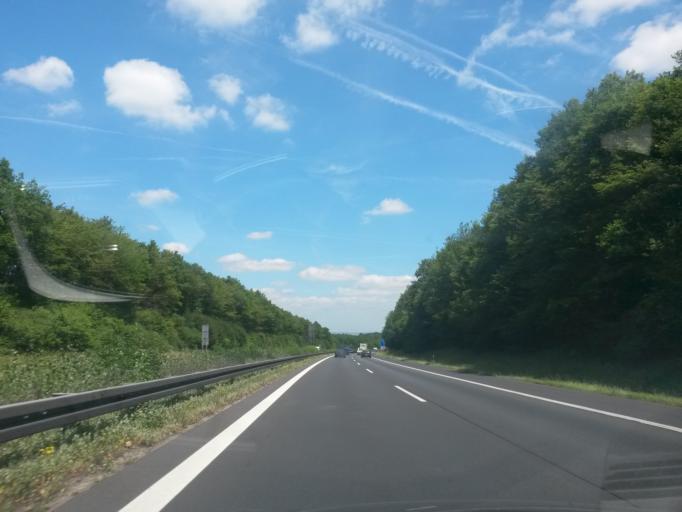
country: DE
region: Bavaria
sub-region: Regierungsbezirk Unterfranken
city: Arnstein
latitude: 49.9362
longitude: 10.0043
